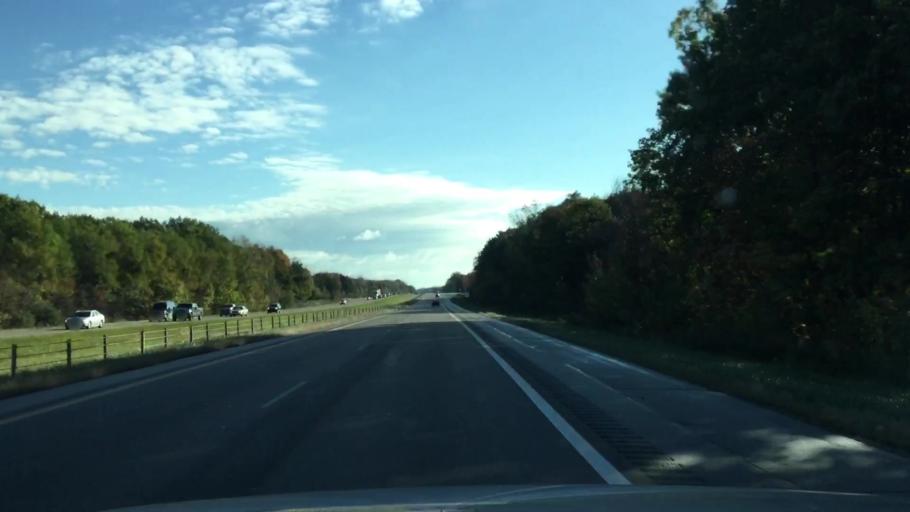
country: US
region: Michigan
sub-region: Genesee County
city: Swartz Creek
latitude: 42.9646
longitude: -83.8777
